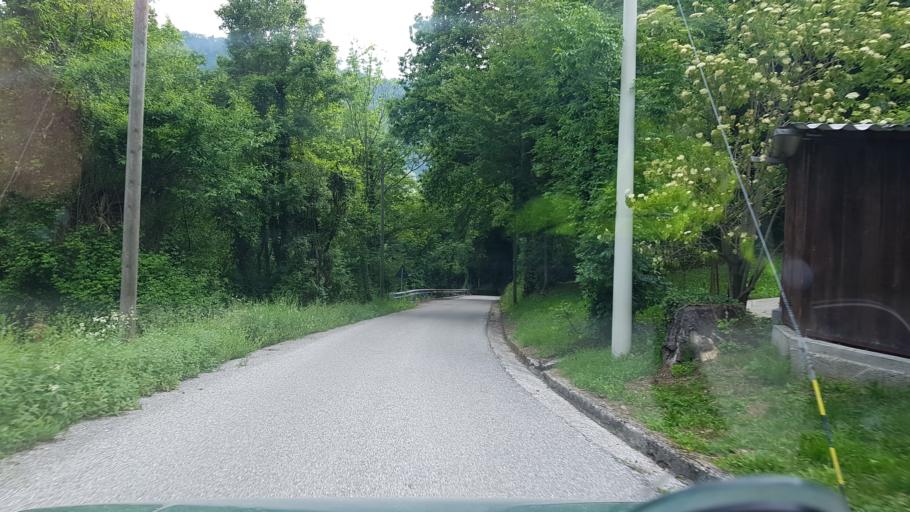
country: IT
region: Friuli Venezia Giulia
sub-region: Provincia di Udine
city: Pulfero
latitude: 46.1822
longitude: 13.4567
